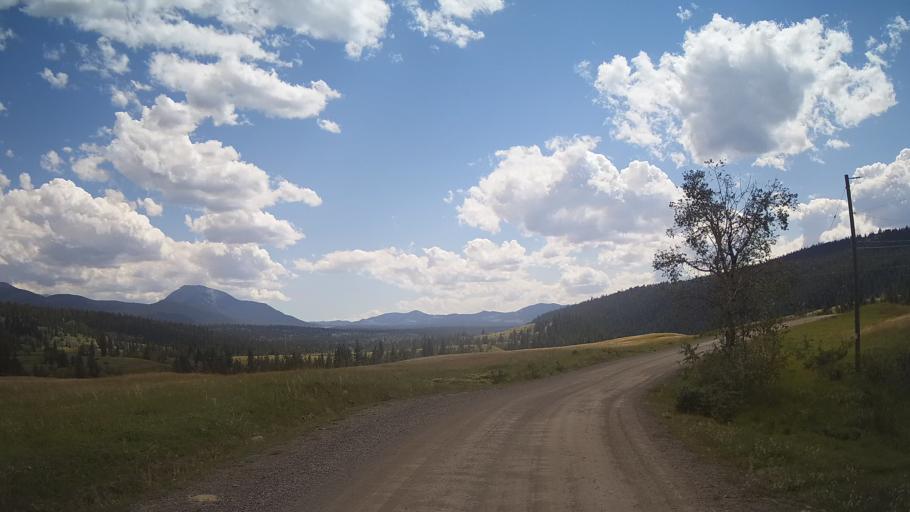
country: CA
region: British Columbia
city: Lillooet
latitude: 51.3102
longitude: -121.9845
